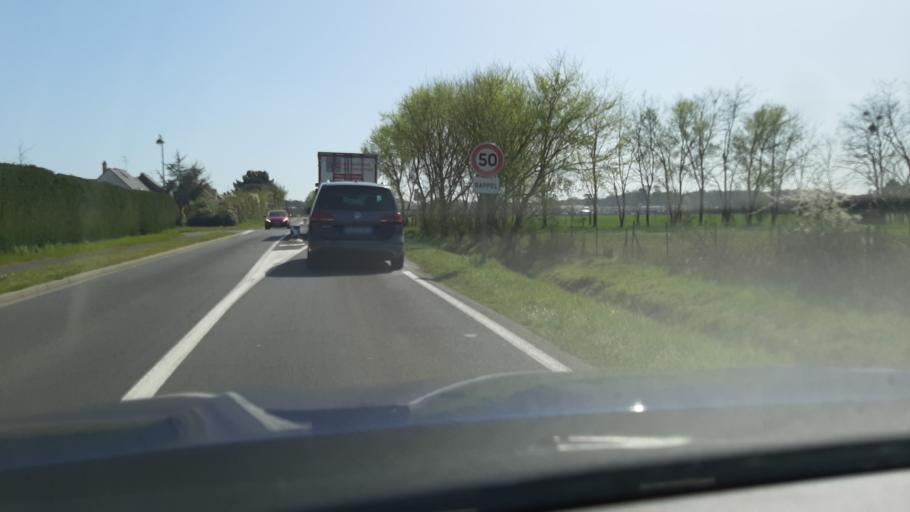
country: FR
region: Pays de la Loire
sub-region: Departement de Maine-et-Loire
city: Pellouailles-les-Vignes
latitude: 47.5172
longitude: -0.4815
